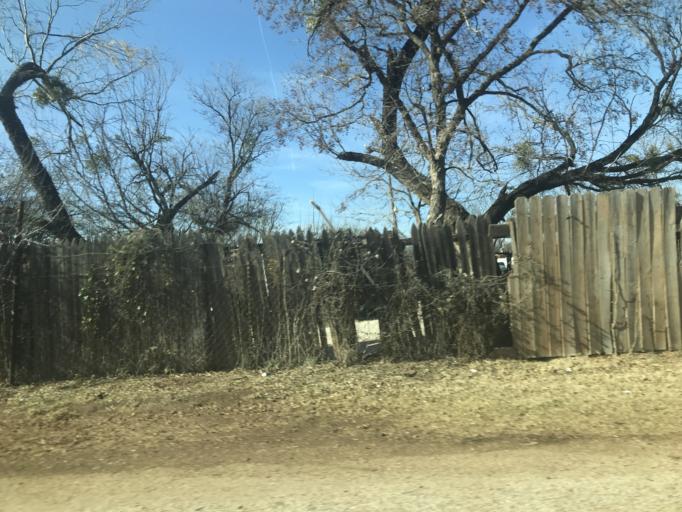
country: US
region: Texas
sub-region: Taylor County
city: Abilene
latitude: 32.4972
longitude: -99.7426
